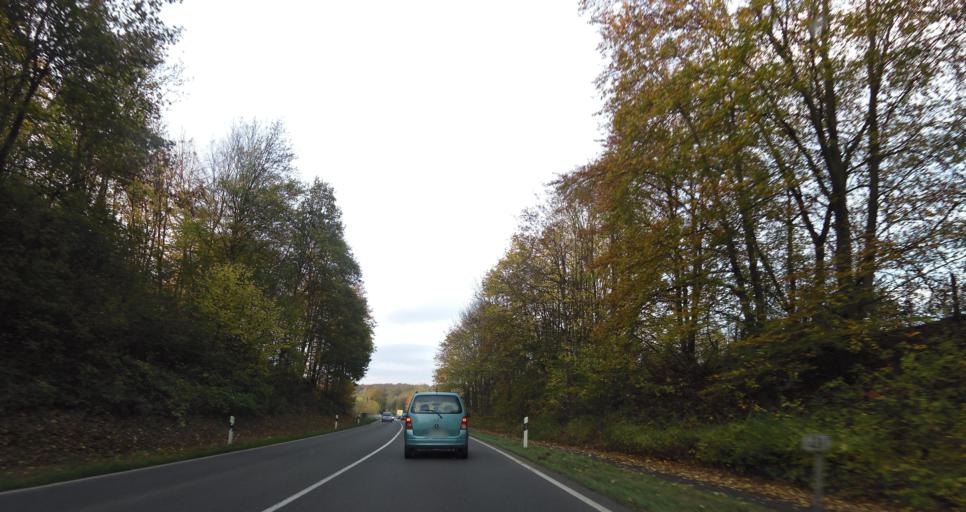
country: DE
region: Lower Saxony
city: Einbeck
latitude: 51.8441
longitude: 9.8436
